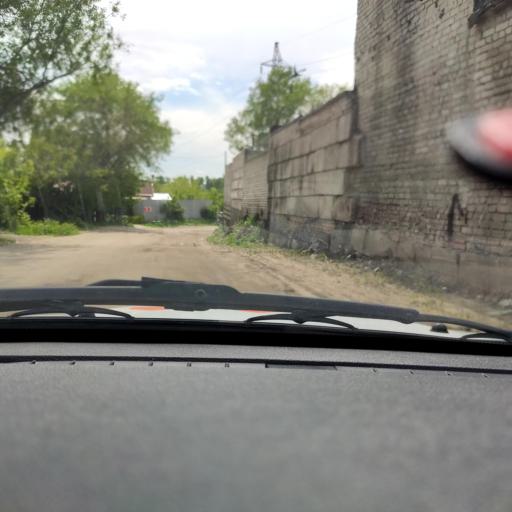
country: RU
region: Voronezj
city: Voronezh
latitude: 51.6345
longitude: 39.1573
